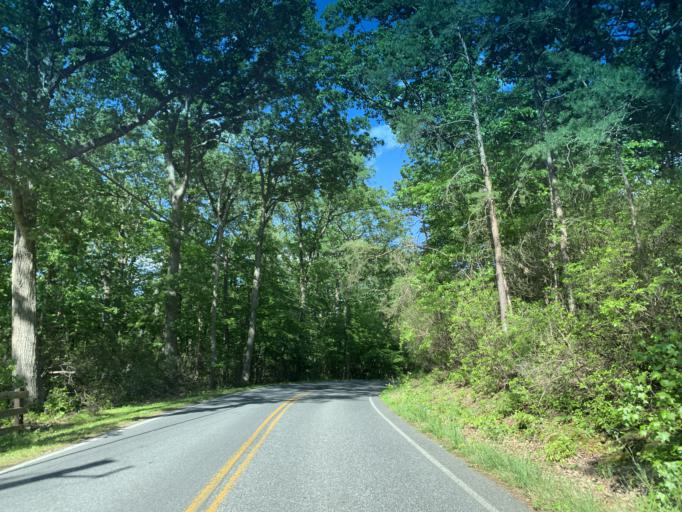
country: US
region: Maryland
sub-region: Cecil County
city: North East
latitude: 39.5409
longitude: -75.9216
